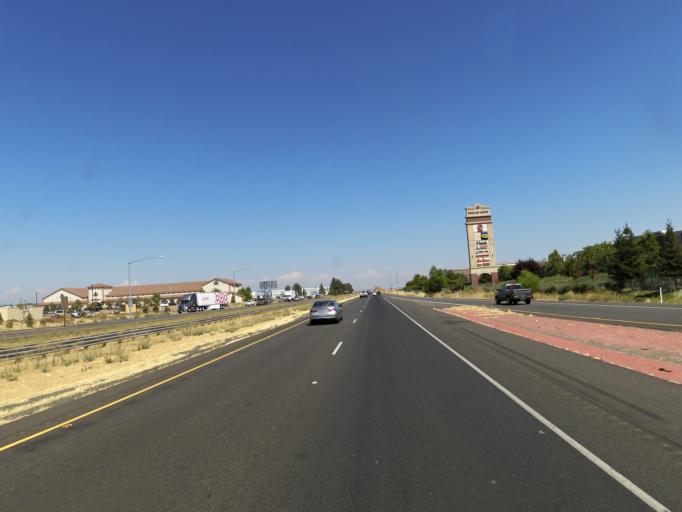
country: US
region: California
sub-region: Yolo County
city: Woodland
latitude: 38.6737
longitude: -121.7256
